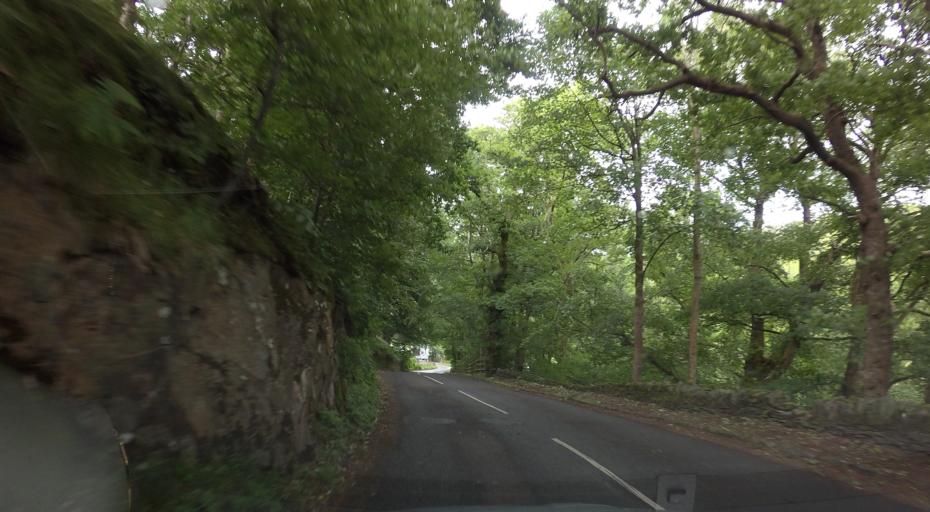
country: GB
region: England
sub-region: Cumbria
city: Keswick
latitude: 54.5214
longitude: -3.1469
